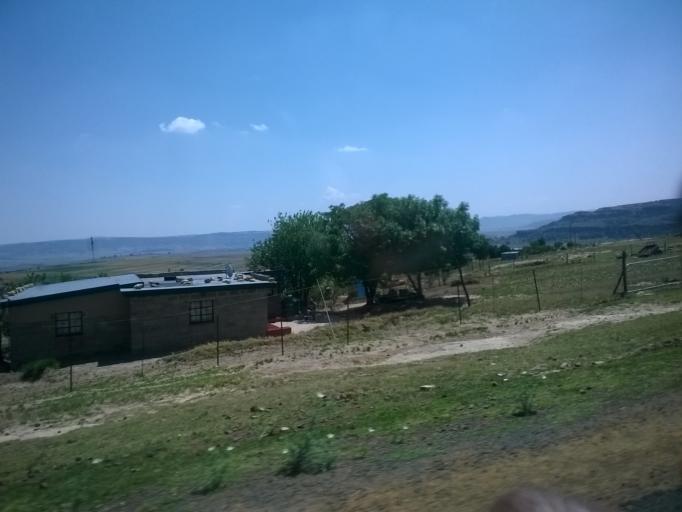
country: LS
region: Berea
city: Teyateyaneng
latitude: -29.1163
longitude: 27.8071
